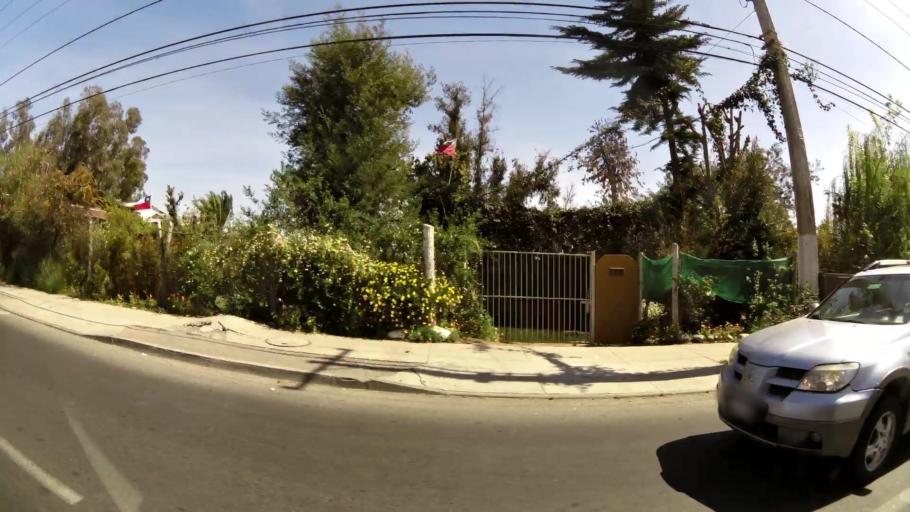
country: CL
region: Santiago Metropolitan
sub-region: Provincia de Cordillera
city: Puente Alto
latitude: -33.5887
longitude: -70.5425
